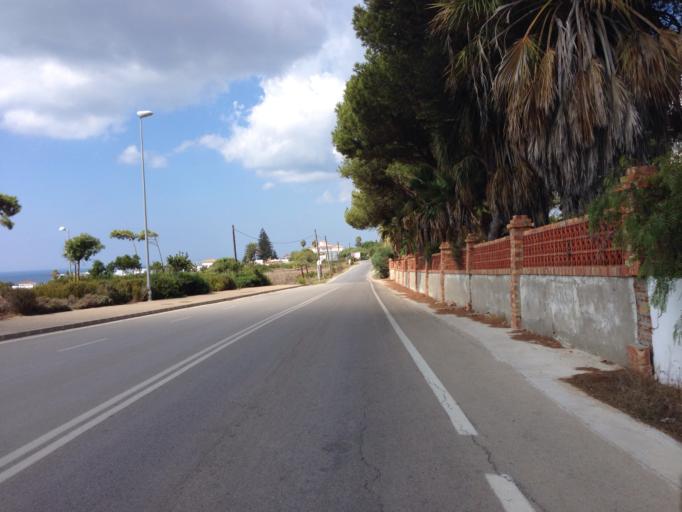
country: ES
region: Andalusia
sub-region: Provincia de Cadiz
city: Conil de la Frontera
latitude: 36.2871
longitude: -6.0989
